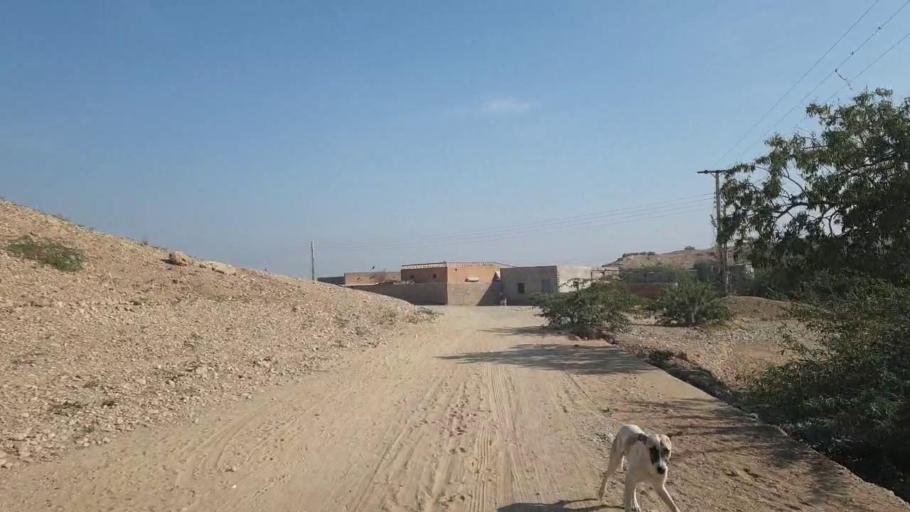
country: PK
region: Sindh
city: Matiari
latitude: 25.6240
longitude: 68.3165
